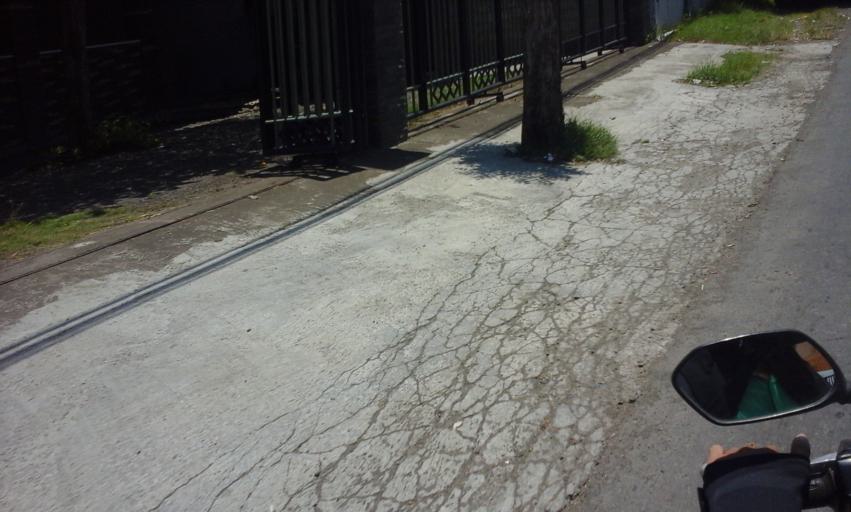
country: ID
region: East Java
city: Sumberdangdang
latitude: -8.1919
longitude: 113.7100
